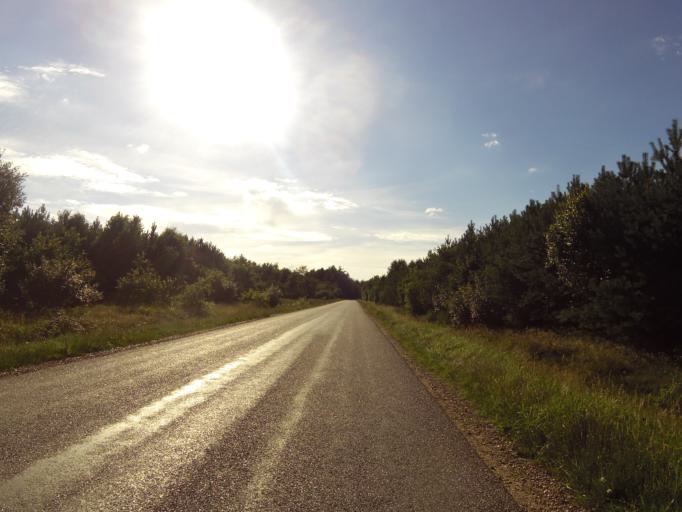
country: DK
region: South Denmark
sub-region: Haderslev Kommune
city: Vojens
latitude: 55.2104
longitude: 9.2444
